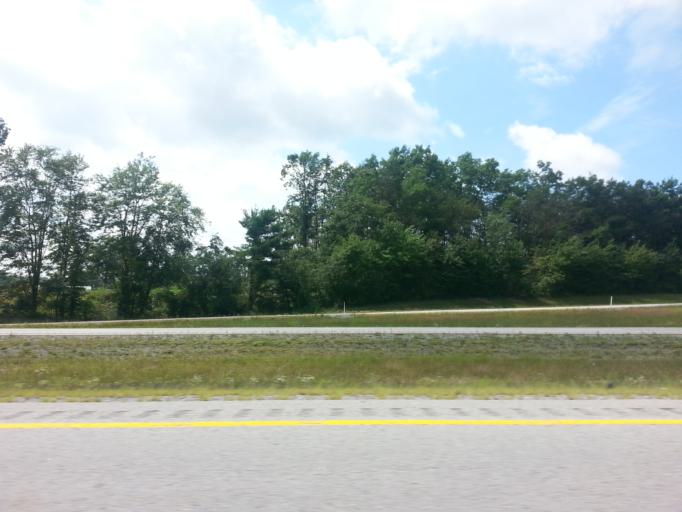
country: US
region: Tennessee
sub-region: Cumberland County
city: Crossville
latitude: 35.9612
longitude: -84.9808
